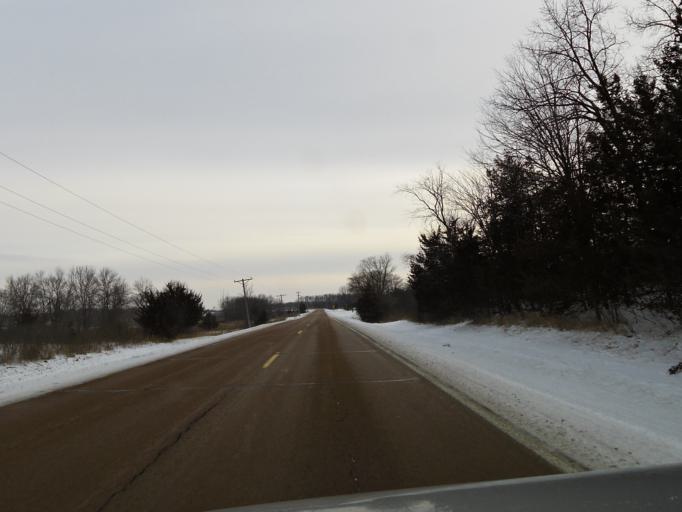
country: US
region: Minnesota
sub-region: Hennepin County
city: Saint Bonifacius
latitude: 44.8859
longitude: -93.7043
